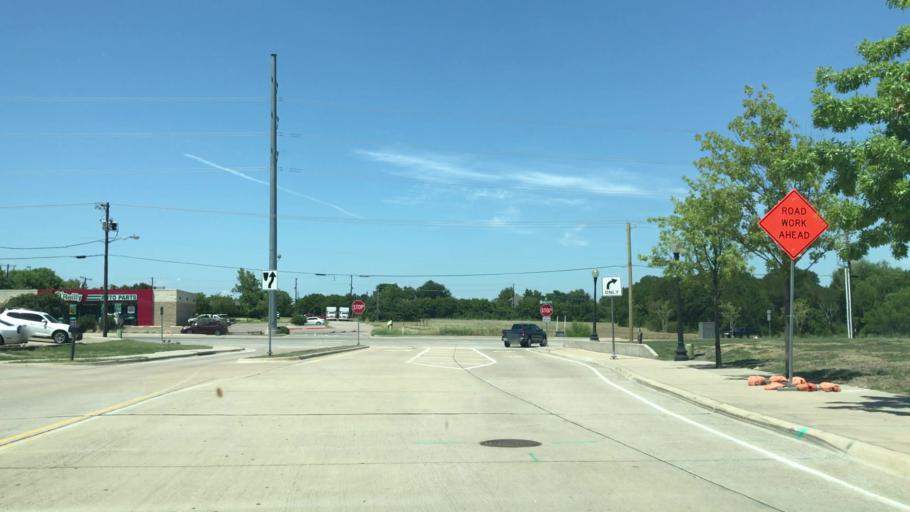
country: US
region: Texas
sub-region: Dallas County
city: Rowlett
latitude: 32.9069
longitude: -96.5637
